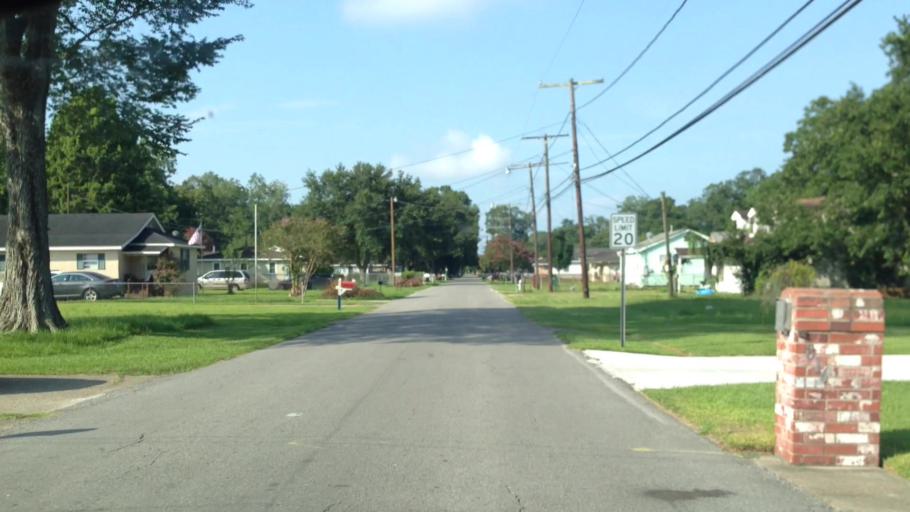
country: US
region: Louisiana
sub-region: Jefferson Parish
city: Bridge City
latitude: 29.9376
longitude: -90.1565
